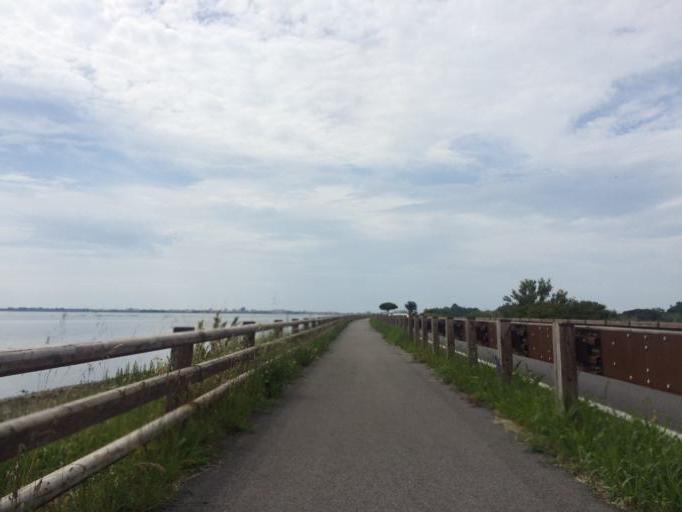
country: IT
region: Friuli Venezia Giulia
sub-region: Provincia di Gorizia
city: Grado
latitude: 45.7190
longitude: 13.3854
